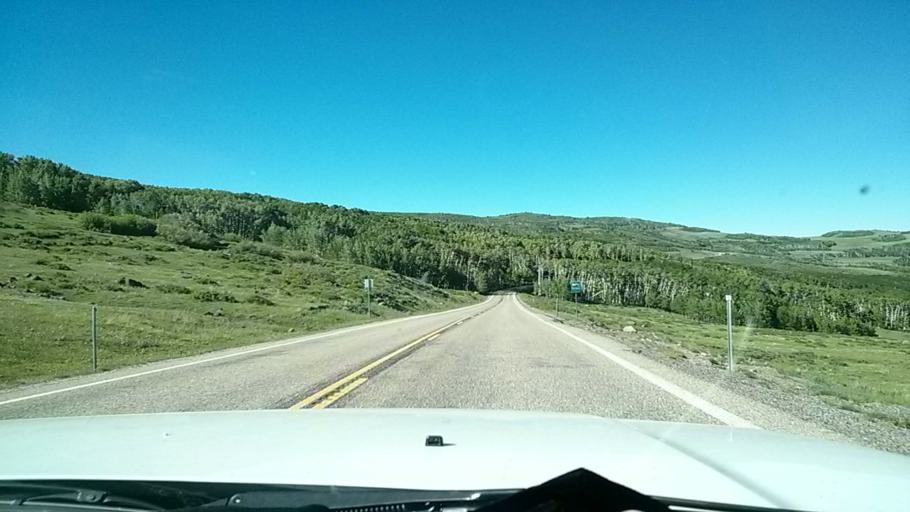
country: US
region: Utah
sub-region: Wayne County
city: Loa
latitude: 38.0146
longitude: -111.3577
